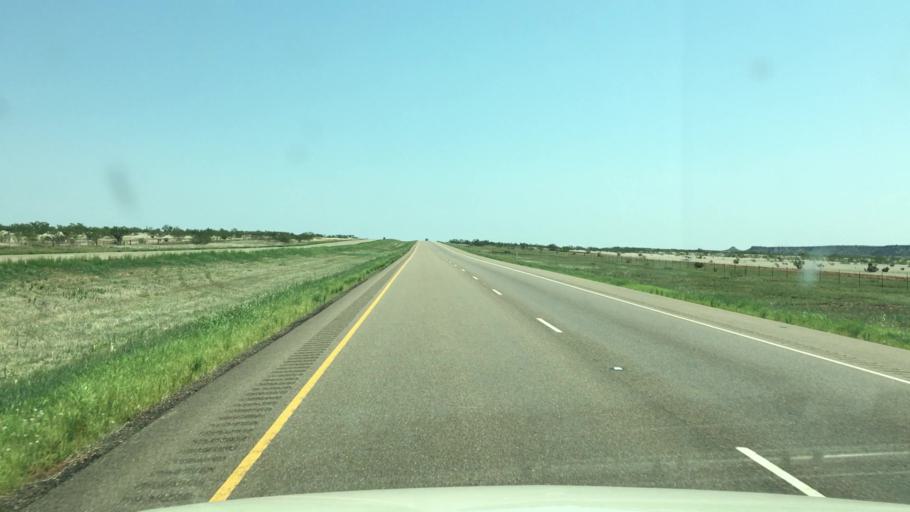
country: US
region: Texas
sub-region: Oldham County
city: Vega
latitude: 35.2233
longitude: -102.8789
